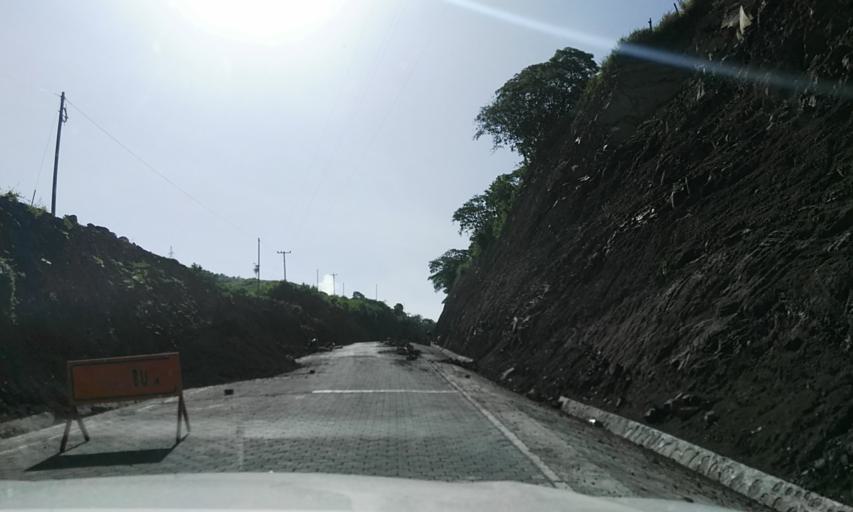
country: NI
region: Matagalpa
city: Terrabona
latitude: 12.7541
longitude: -85.9827
